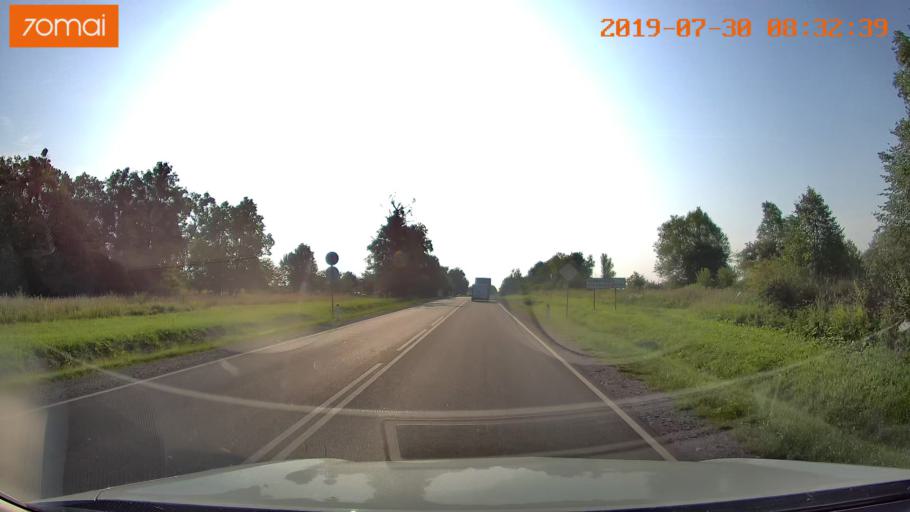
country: RU
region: Kaliningrad
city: Chernyakhovsk
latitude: 54.6373
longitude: 21.7323
